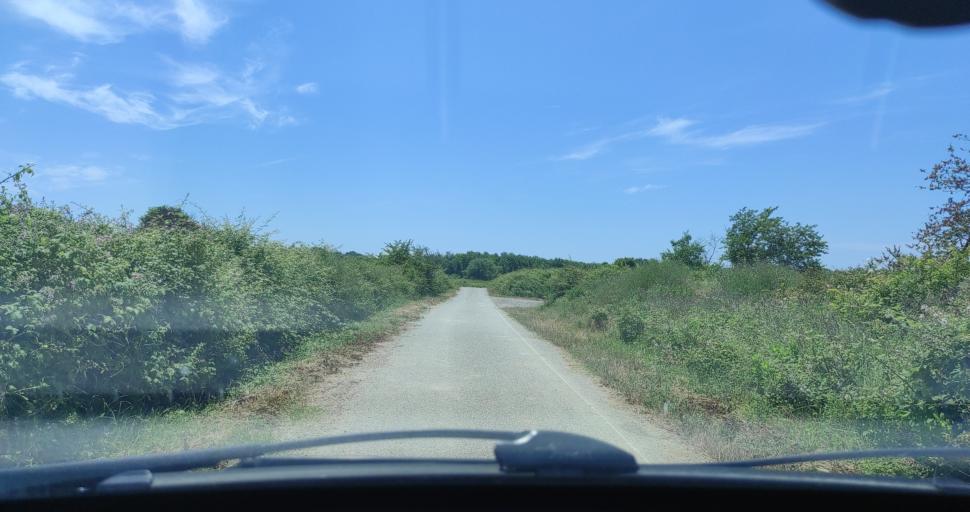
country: AL
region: Shkoder
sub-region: Rrethi i Shkodres
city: Velipoje
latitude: 41.8825
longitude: 19.3844
